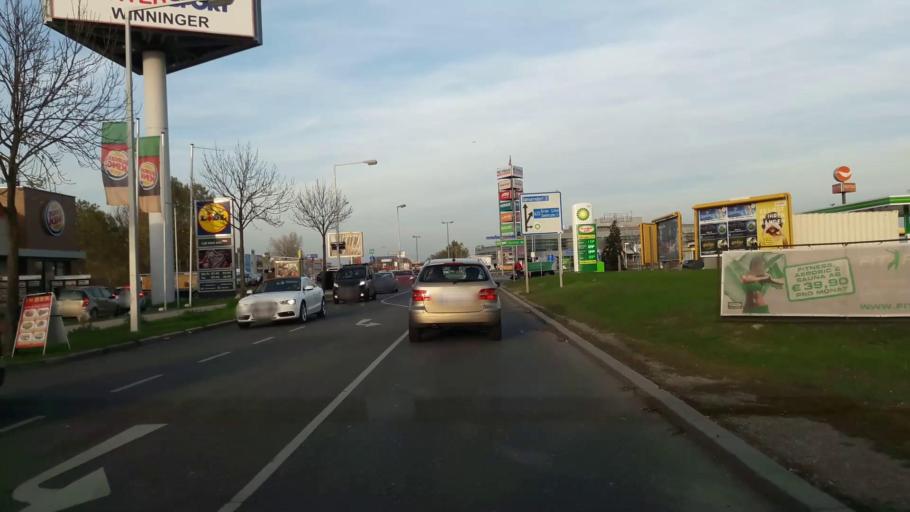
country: AT
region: Lower Austria
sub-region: Politischer Bezirk Wien-Umgebung
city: Gerasdorf bei Wien
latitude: 48.2472
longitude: 16.4650
